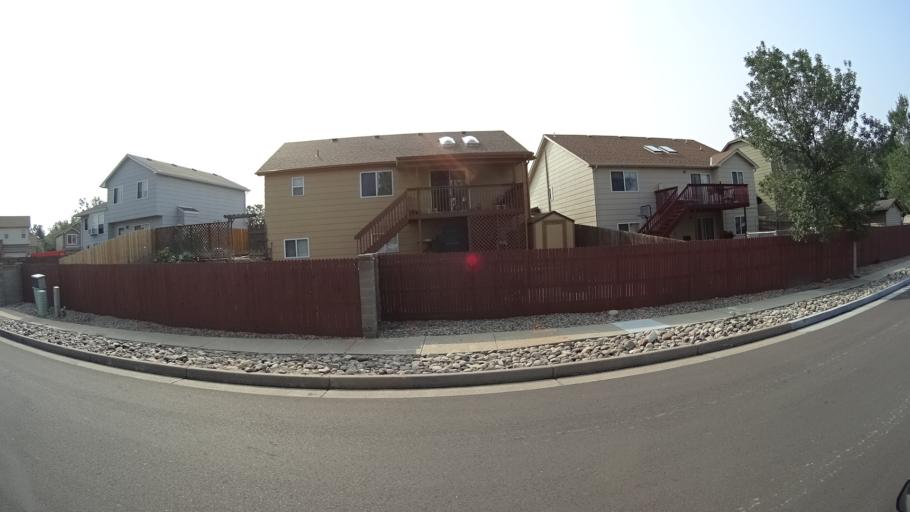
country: US
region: Colorado
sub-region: El Paso County
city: Stratmoor
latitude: 38.8215
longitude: -104.7518
